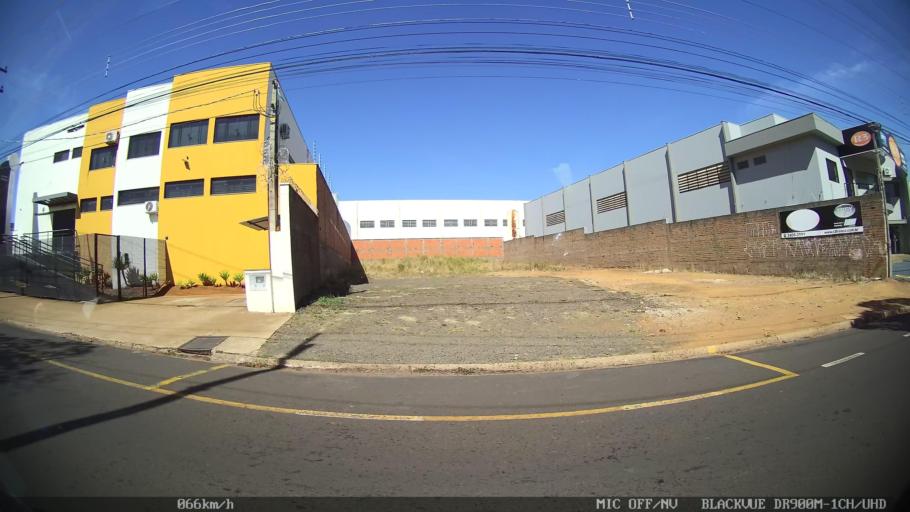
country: BR
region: Sao Paulo
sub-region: Franca
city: Franca
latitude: -20.5462
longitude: -47.4307
